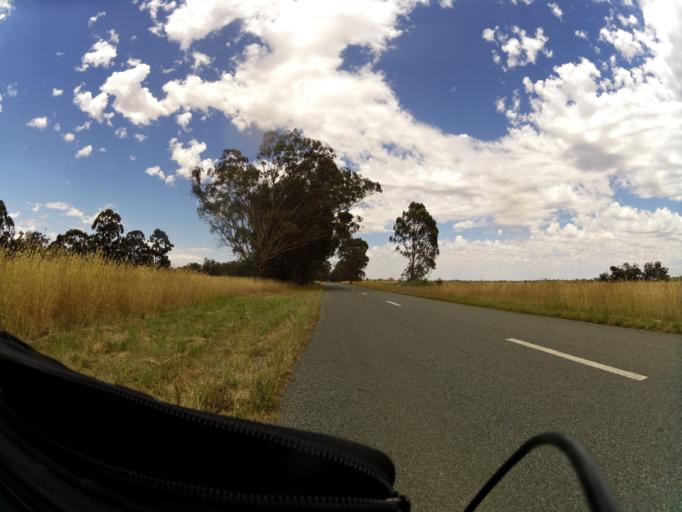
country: AU
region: Victoria
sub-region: Greater Shepparton
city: Shepparton
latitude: -36.6575
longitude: 145.2002
